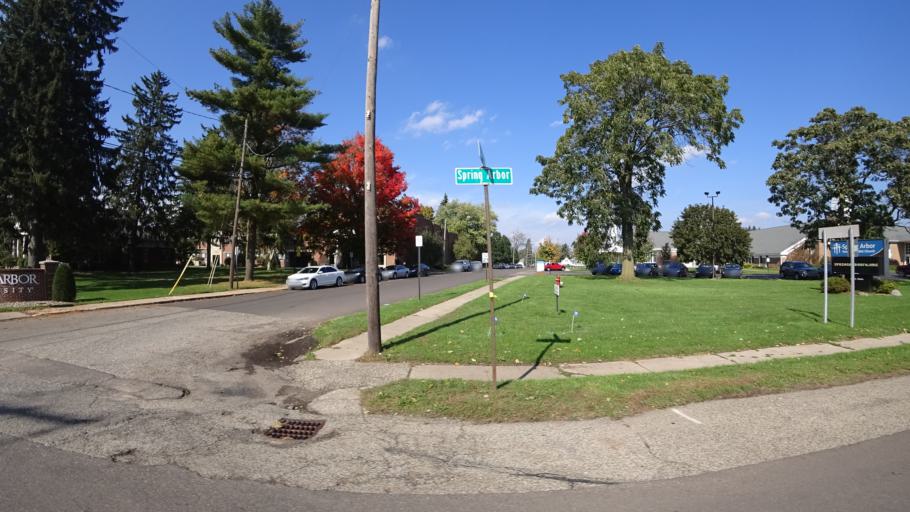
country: US
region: Michigan
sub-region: Jackson County
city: Spring Arbor
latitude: 42.2054
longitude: -84.5530
